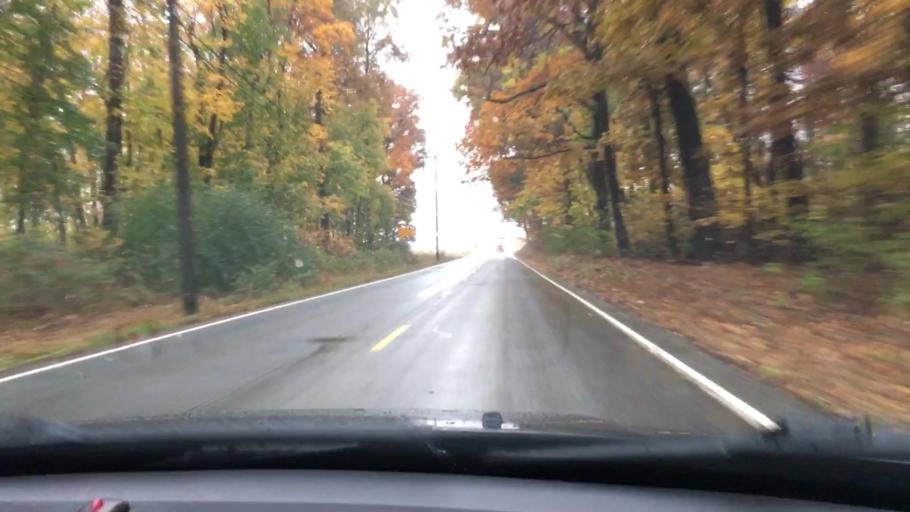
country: US
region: Pennsylvania
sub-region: York County
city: Stewartstown
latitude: 39.7235
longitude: -76.5342
